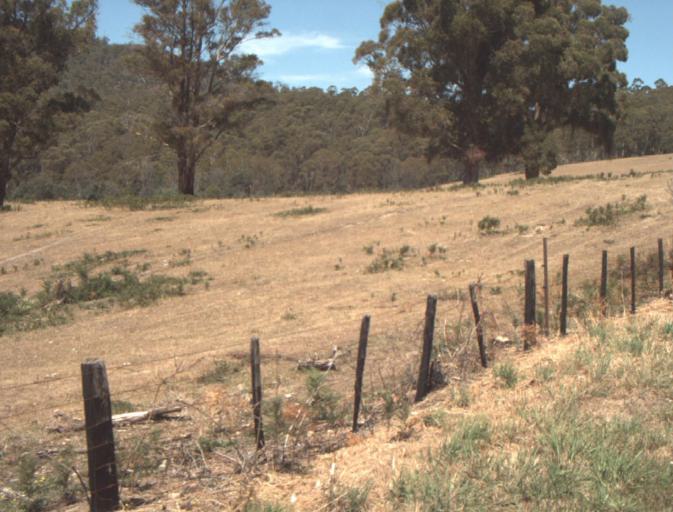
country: AU
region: Tasmania
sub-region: Launceston
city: Mayfield
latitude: -41.2708
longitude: 147.1285
